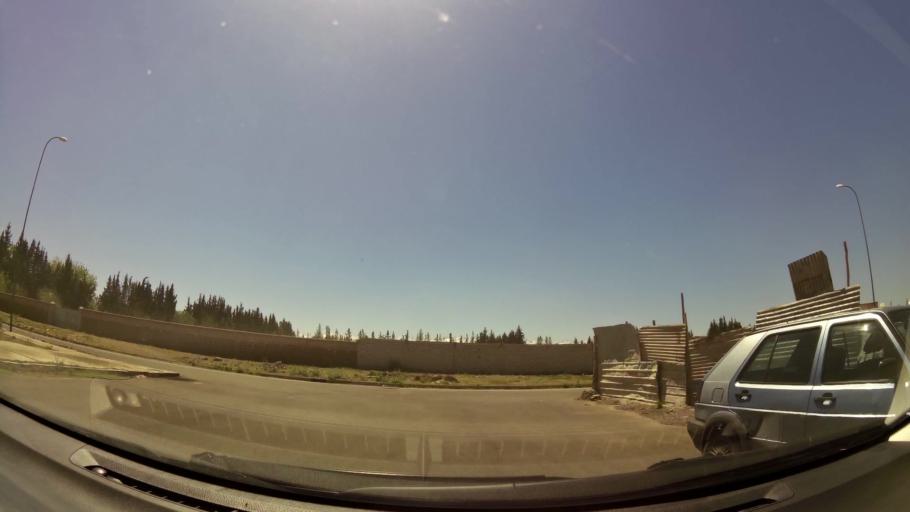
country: MA
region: Marrakech-Tensift-Al Haouz
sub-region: Marrakech
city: Marrakesh
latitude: 31.5501
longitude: -7.9774
